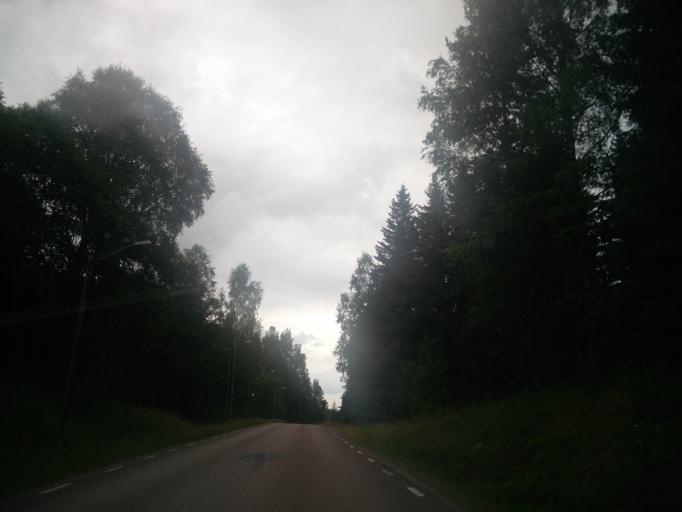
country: SE
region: Vaermland
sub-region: Arvika Kommun
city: Arvika
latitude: 59.8939
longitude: 12.6349
